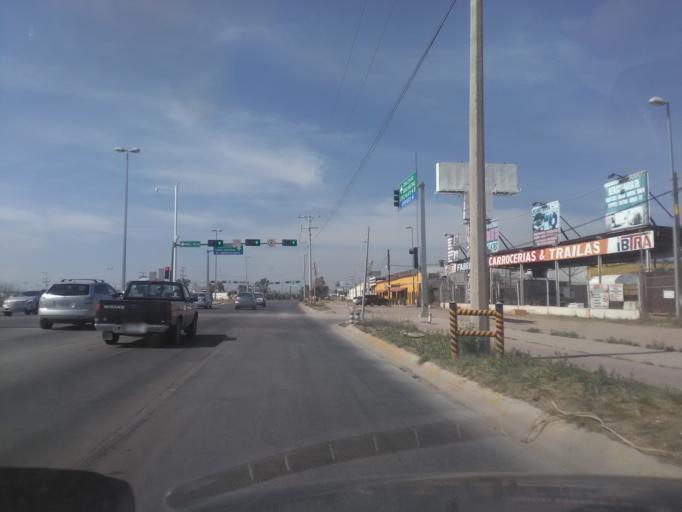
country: MX
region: Durango
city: Victoria de Durango
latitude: 24.0760
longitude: -104.5920
